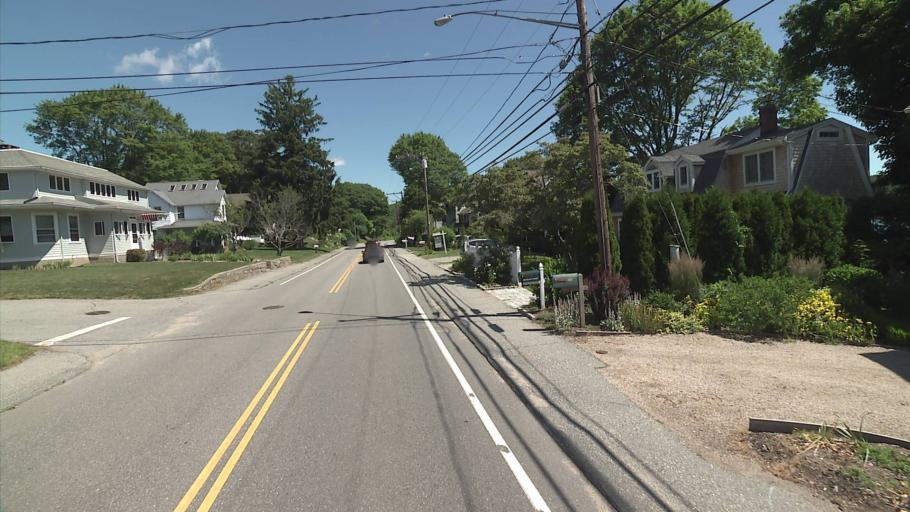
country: US
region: Connecticut
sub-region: New London County
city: Noank
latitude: 41.3350
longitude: -71.9924
